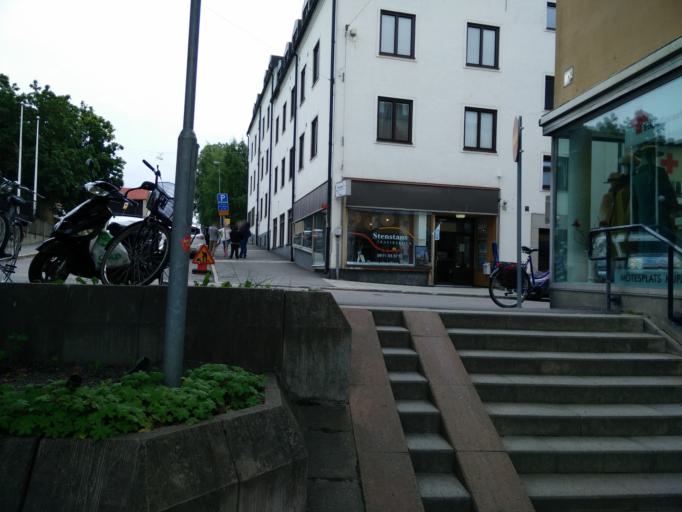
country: SE
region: Vaesternorrland
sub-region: Haernoesands Kommun
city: Haernoesand
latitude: 62.6338
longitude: 17.9406
